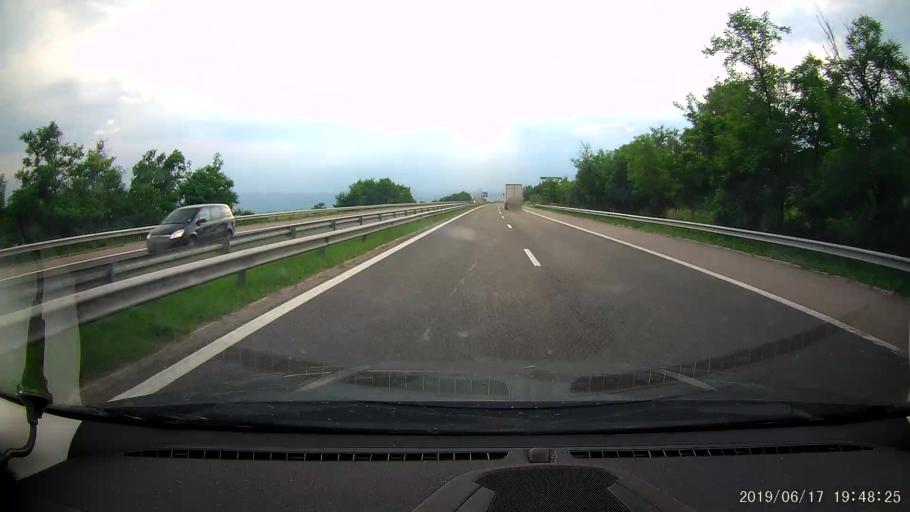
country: BG
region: Sofiya
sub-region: Obshtina Ikhtiman
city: Ikhtiman
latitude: 42.4665
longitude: 23.8233
